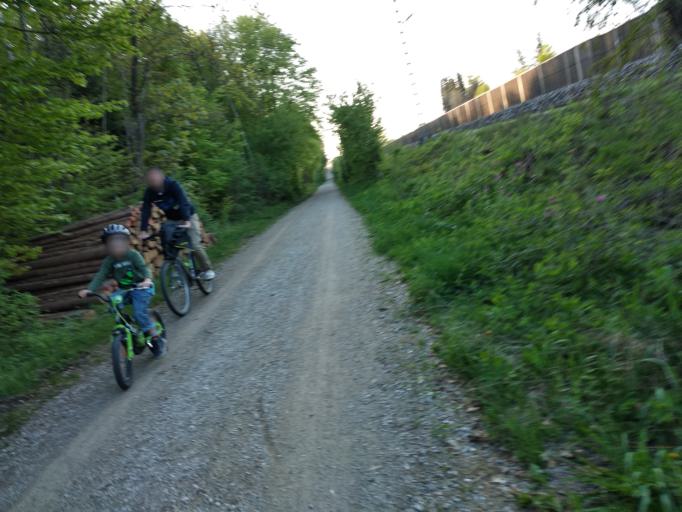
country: DE
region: Bavaria
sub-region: Upper Bavaria
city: Kirchseeon
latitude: 48.0768
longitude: 11.8768
